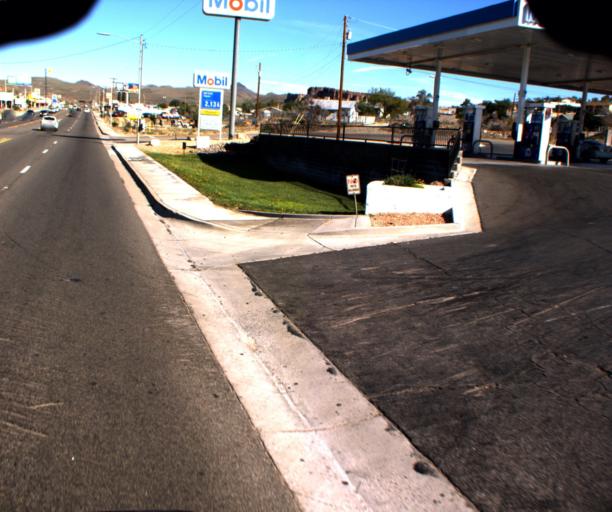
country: US
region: Arizona
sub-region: Mohave County
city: Kingman
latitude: 35.1929
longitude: -114.0714
